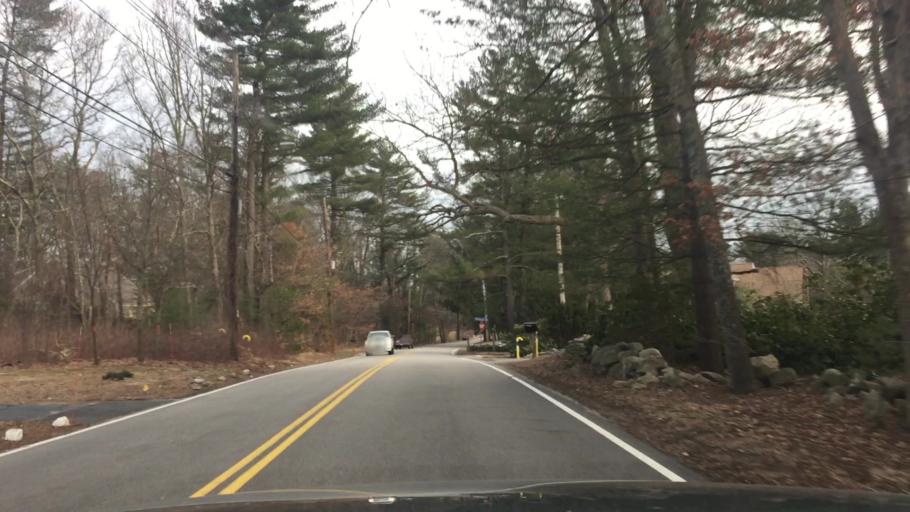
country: US
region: Massachusetts
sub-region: Norfolk County
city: Medway
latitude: 42.1413
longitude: -71.4533
